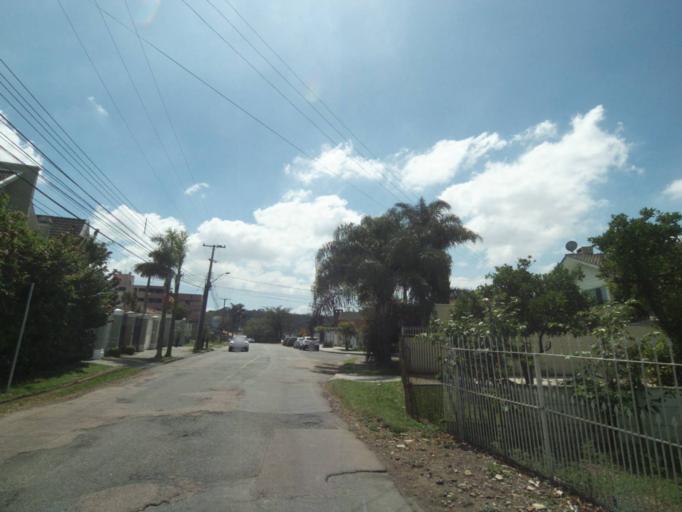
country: BR
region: Parana
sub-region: Curitiba
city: Curitiba
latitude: -25.4119
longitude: -49.2385
